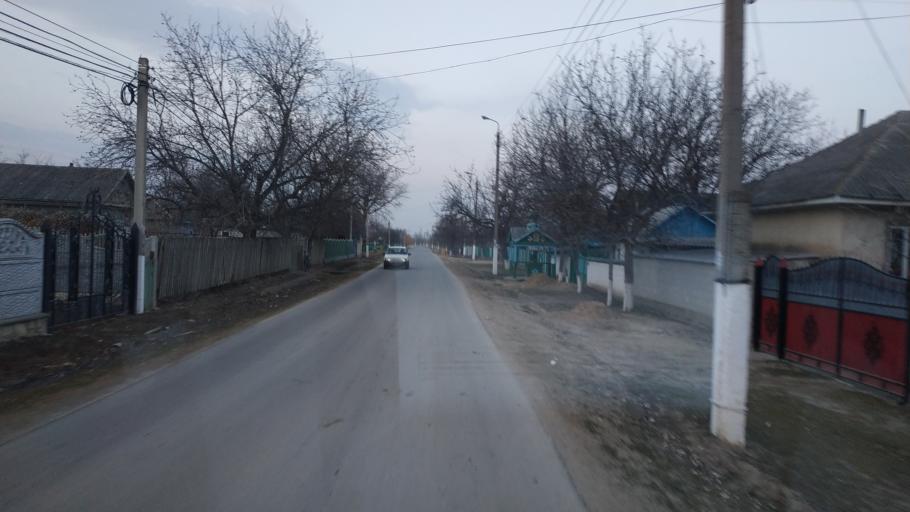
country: RO
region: Vaslui
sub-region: Comuna Stanilesti
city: Stanilesti
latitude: 46.6556
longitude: 28.3058
